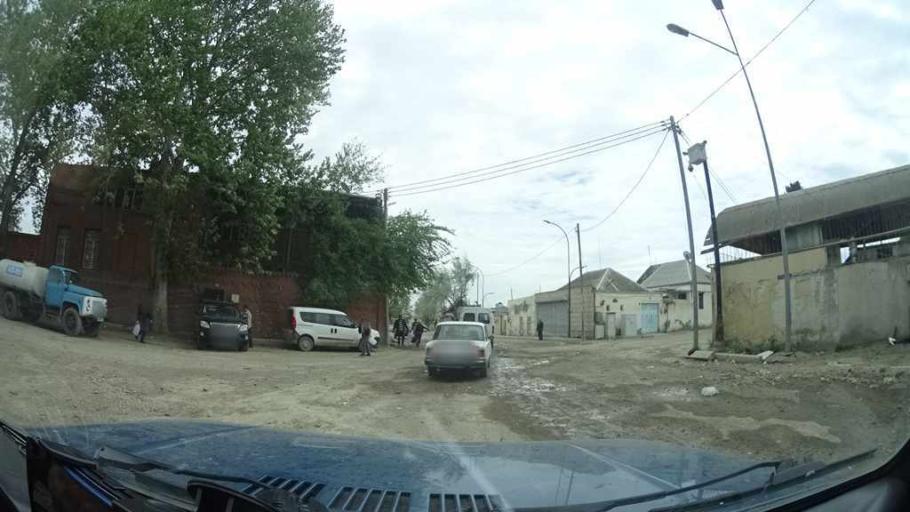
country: AZ
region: Ganja City
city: Ganja
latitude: 40.6766
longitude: 46.3621
